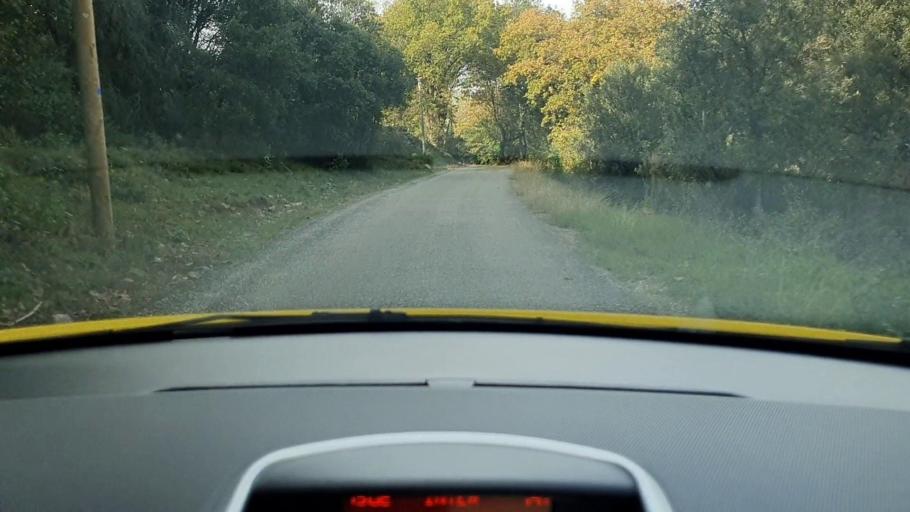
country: FR
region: Languedoc-Roussillon
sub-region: Departement du Gard
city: Anduze
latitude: 44.0358
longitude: 3.9268
